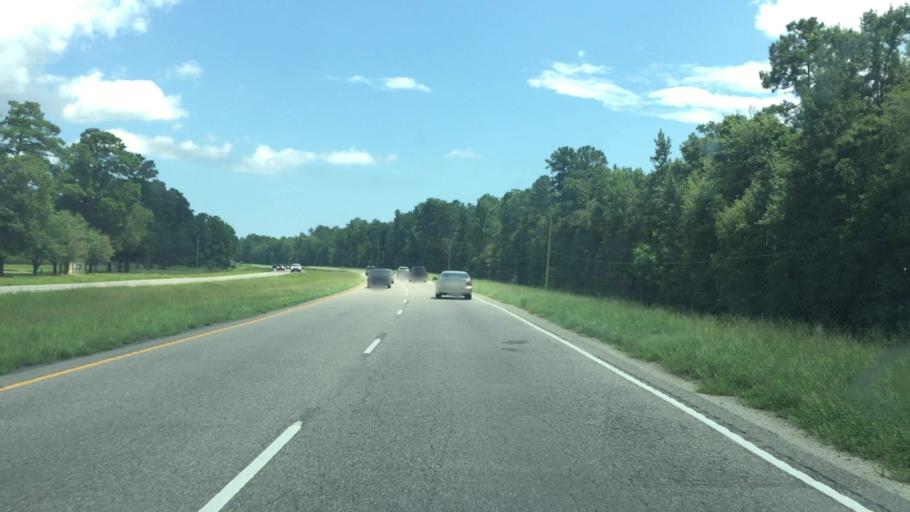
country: US
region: South Carolina
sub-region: Horry County
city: North Myrtle Beach
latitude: 33.9187
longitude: -78.7236
